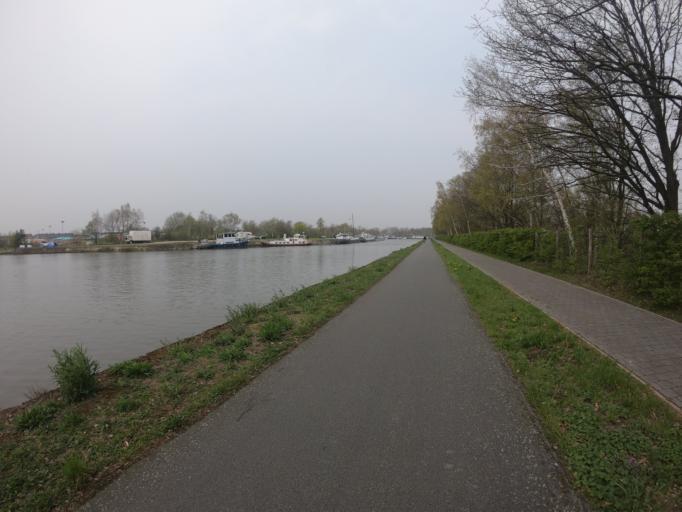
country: BE
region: Flanders
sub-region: Provincie Limburg
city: Maasmechelen
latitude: 50.9857
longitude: 5.7064
